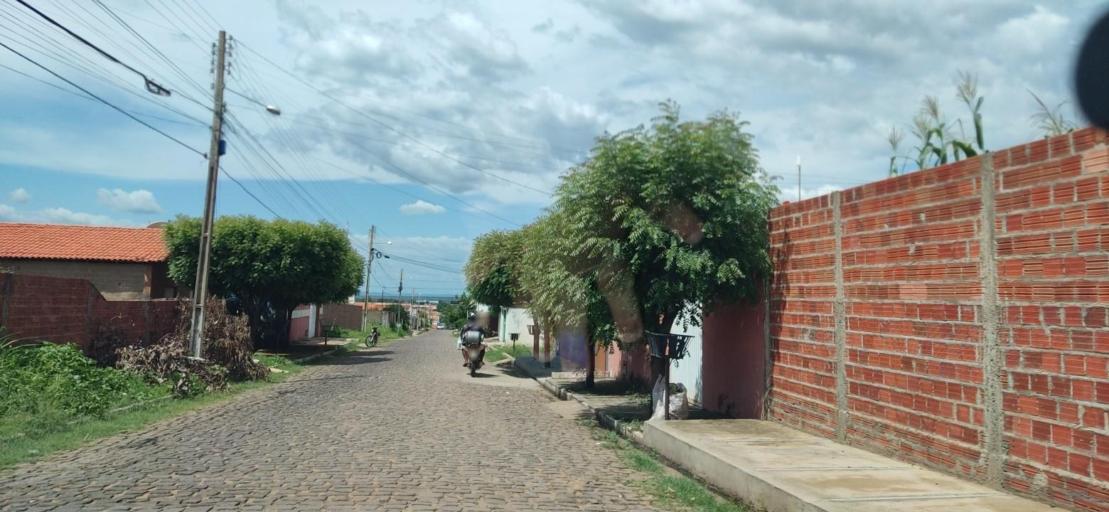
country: BR
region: Piaui
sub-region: Valenca Do Piaui
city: Valenca do Piaui
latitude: -6.4080
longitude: -41.7444
